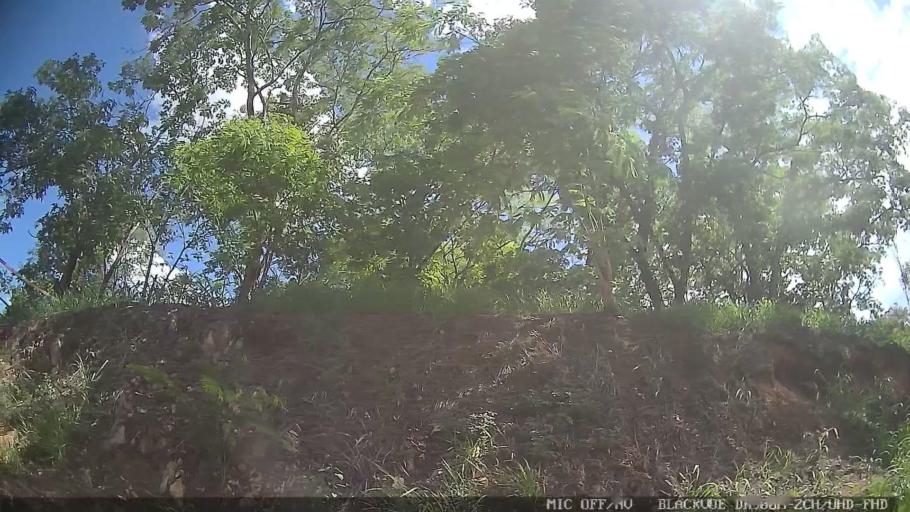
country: BR
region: Sao Paulo
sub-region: Pedreira
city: Pedreira
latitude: -22.7426
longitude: -46.9078
